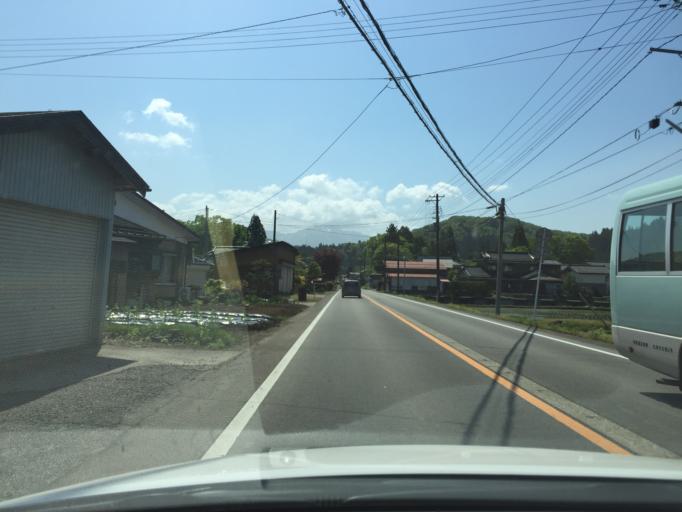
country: JP
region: Niigata
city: Kamo
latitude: 37.6303
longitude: 139.0953
